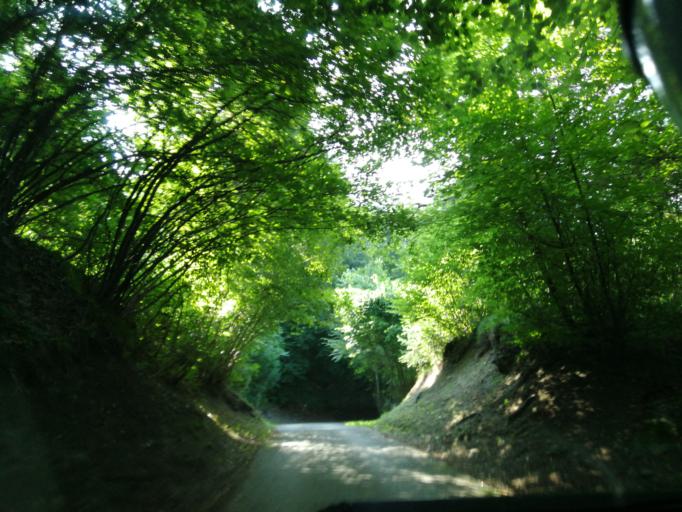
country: IT
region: Trentino-Alto Adige
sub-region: Provincia di Trento
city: Storo
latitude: 45.8288
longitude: 10.5698
